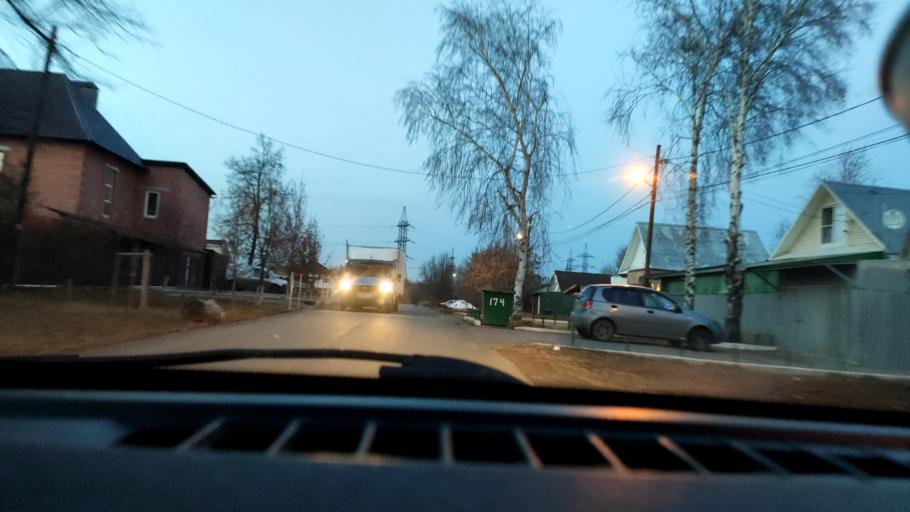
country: RU
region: Samara
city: Petra-Dubrava
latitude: 53.2619
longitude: 50.3300
